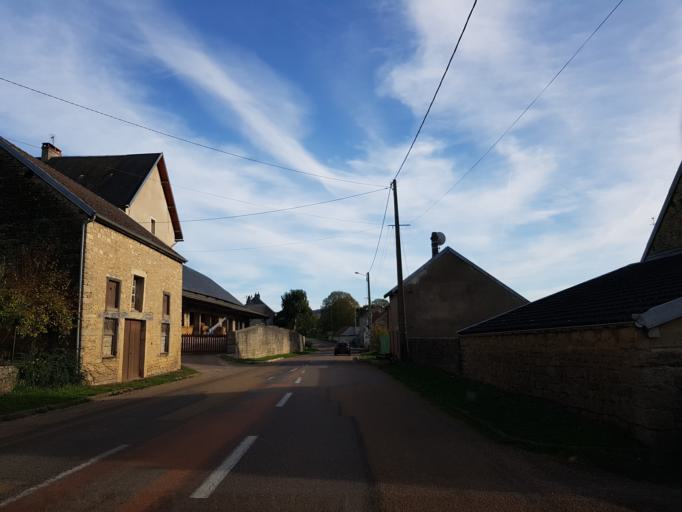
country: FR
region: Bourgogne
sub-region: Departement de la Cote-d'Or
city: Pouilly-en-Auxois
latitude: 47.3207
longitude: 4.5954
